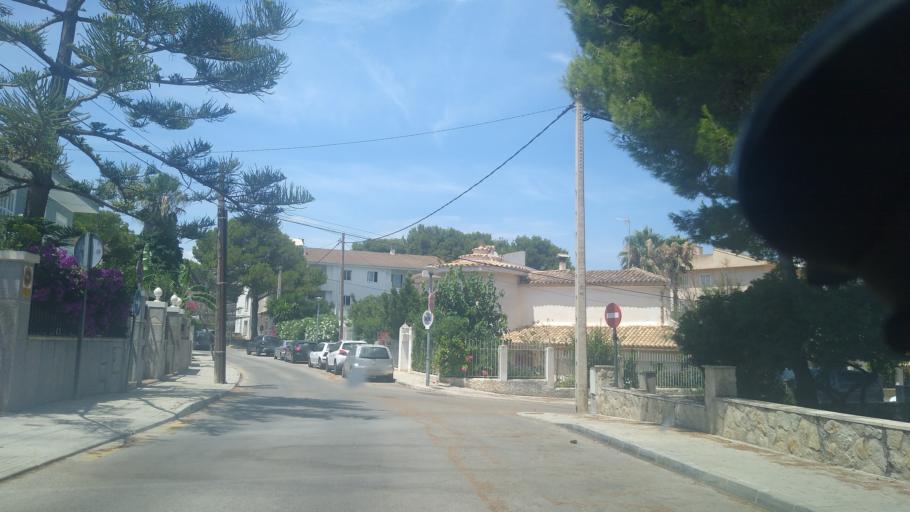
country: ES
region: Balearic Islands
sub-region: Illes Balears
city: Santa Margalida
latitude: 39.7579
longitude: 3.1670
